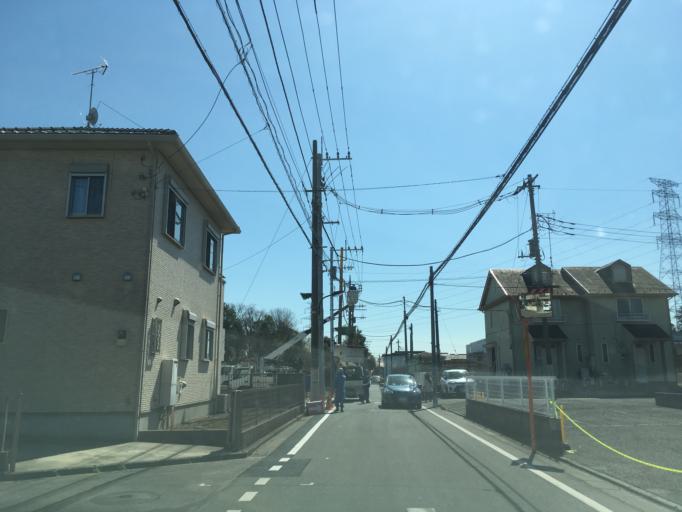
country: JP
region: Tokyo
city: Kokubunji
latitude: 35.7193
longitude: 139.4506
